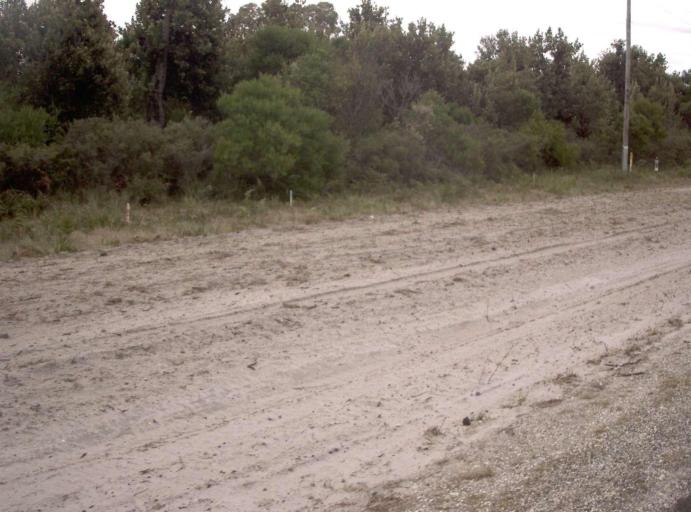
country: AU
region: Victoria
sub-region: East Gippsland
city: Bairnsdale
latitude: -38.0958
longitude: 147.5120
